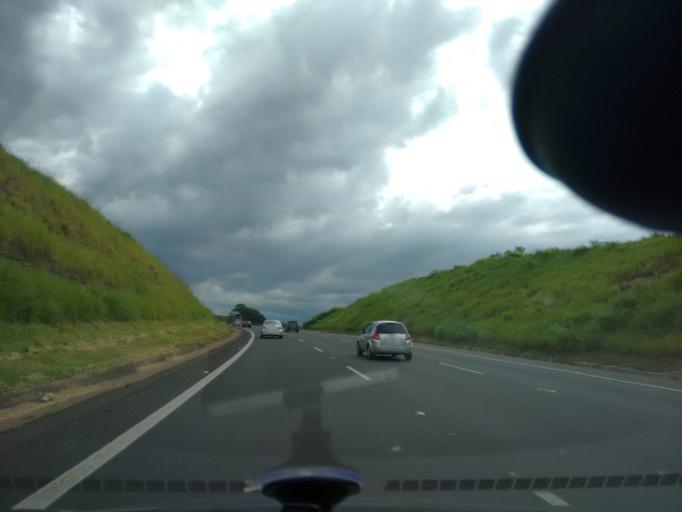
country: BR
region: Sao Paulo
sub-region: Campinas
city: Campinas
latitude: -22.9211
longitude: -47.1345
